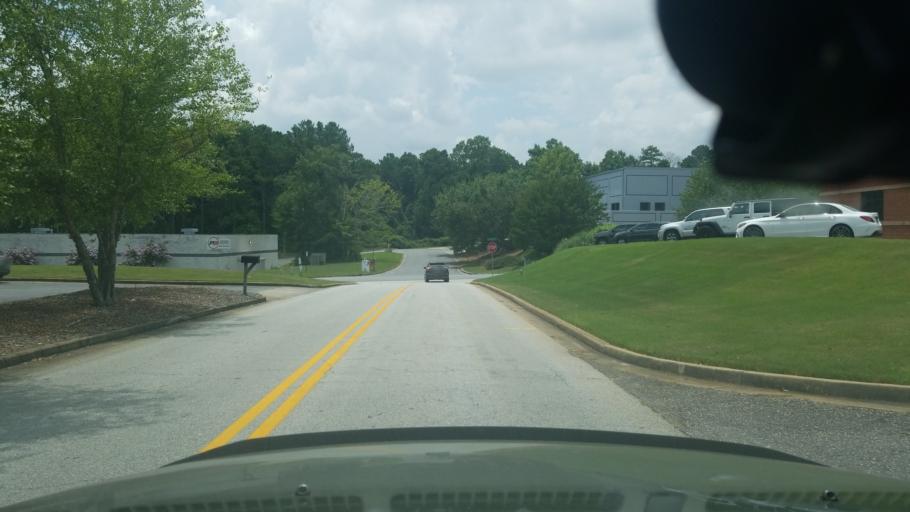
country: US
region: Georgia
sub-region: Fulton County
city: Milton
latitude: 34.1437
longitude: -84.2451
